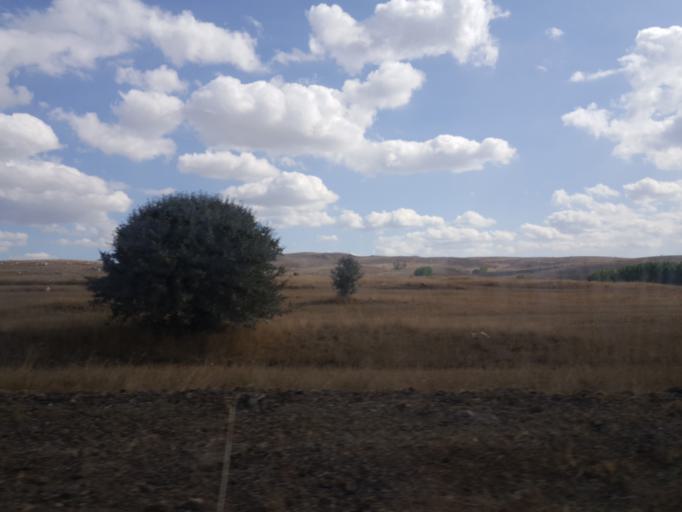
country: TR
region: Tokat
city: Artova
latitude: 40.1467
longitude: 36.3769
